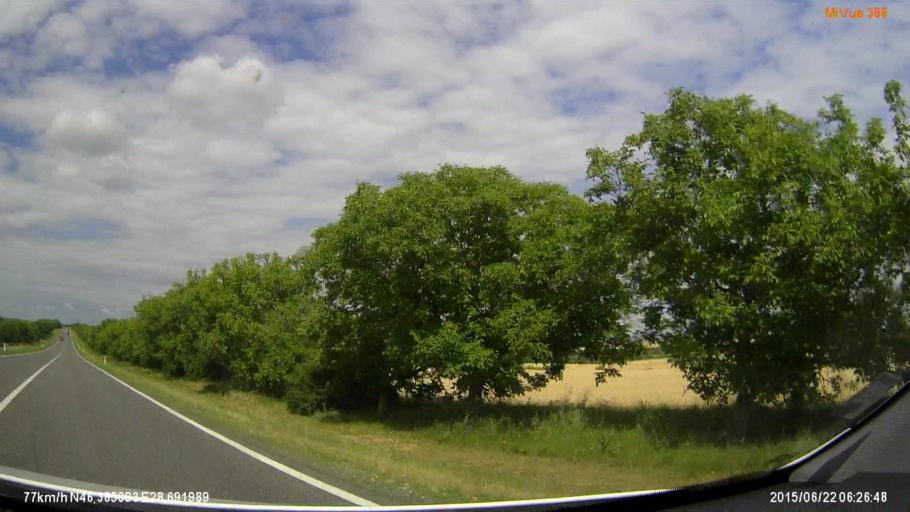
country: MD
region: Gagauzia
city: Bugeac
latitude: 46.3848
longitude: 28.6916
